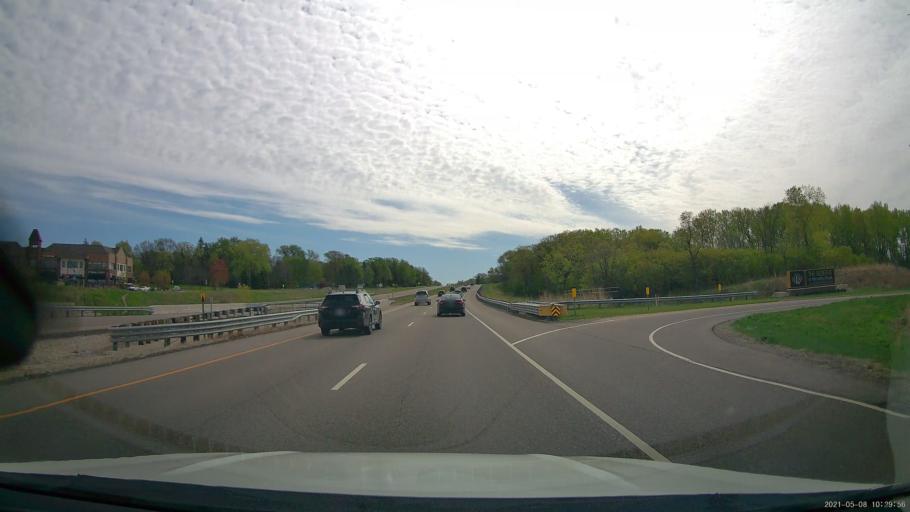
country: US
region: Minnesota
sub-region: Dakota County
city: Mendota Heights
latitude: 44.8828
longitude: -93.1213
